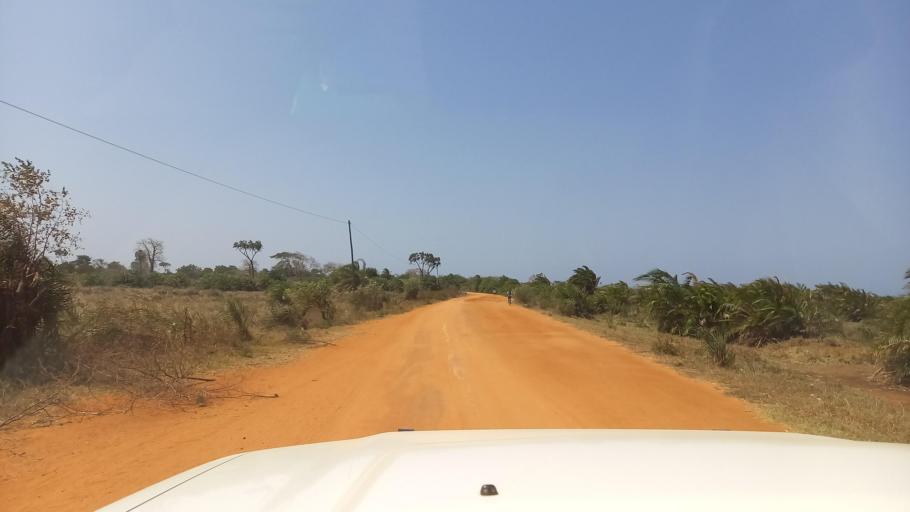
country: MZ
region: Cabo Delgado
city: Pemba
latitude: -13.3902
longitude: 40.5304
